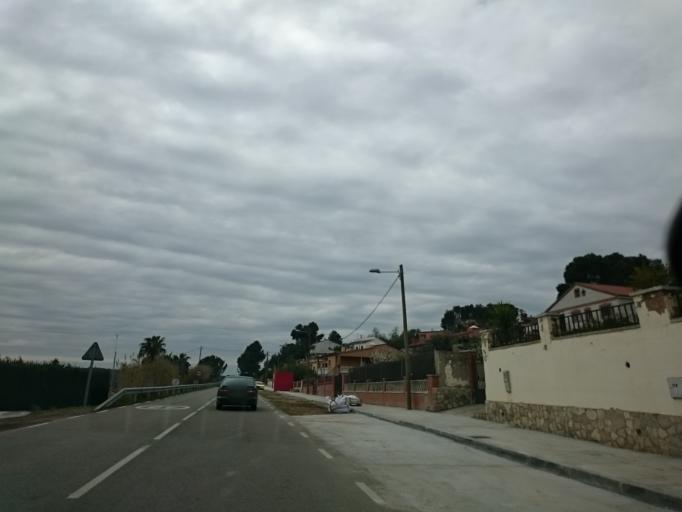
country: ES
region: Catalonia
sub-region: Provincia de Barcelona
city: Piera
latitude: 41.5085
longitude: 1.7300
